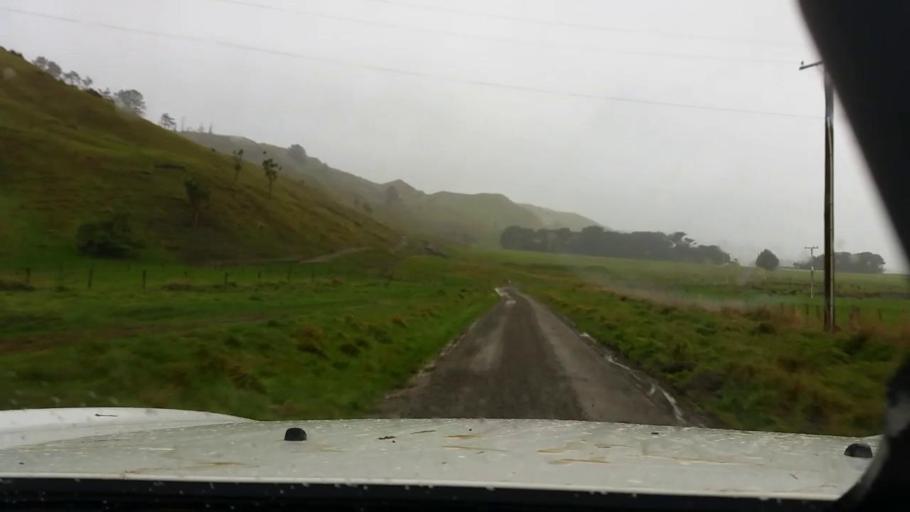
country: NZ
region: Wellington
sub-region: Masterton District
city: Masterton
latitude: -41.2605
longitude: 175.8971
